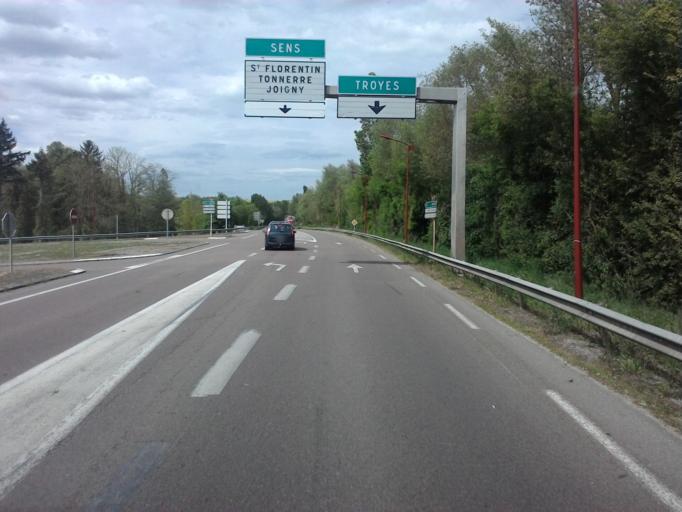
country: FR
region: Bourgogne
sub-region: Departement de l'Yonne
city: Saint-Florentin
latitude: 47.9962
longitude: 3.7352
